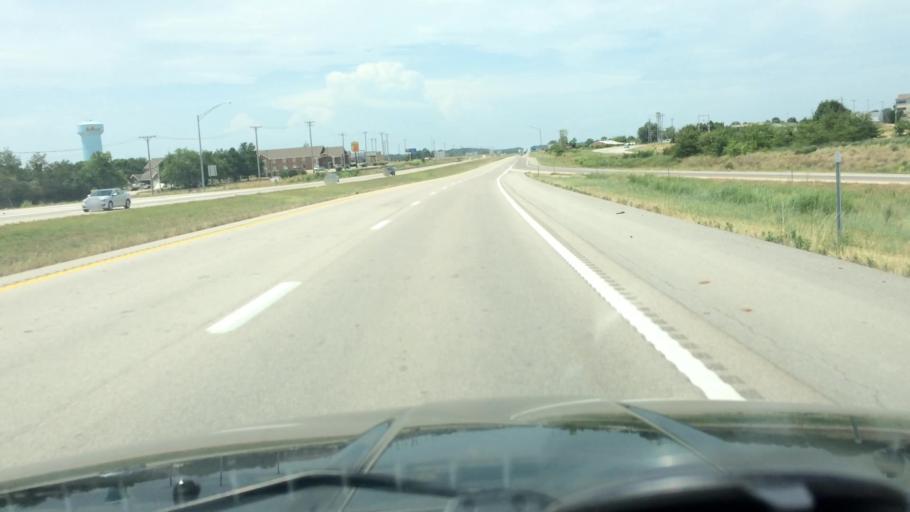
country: US
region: Missouri
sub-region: Polk County
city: Bolivar
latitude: 37.5946
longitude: -93.4336
